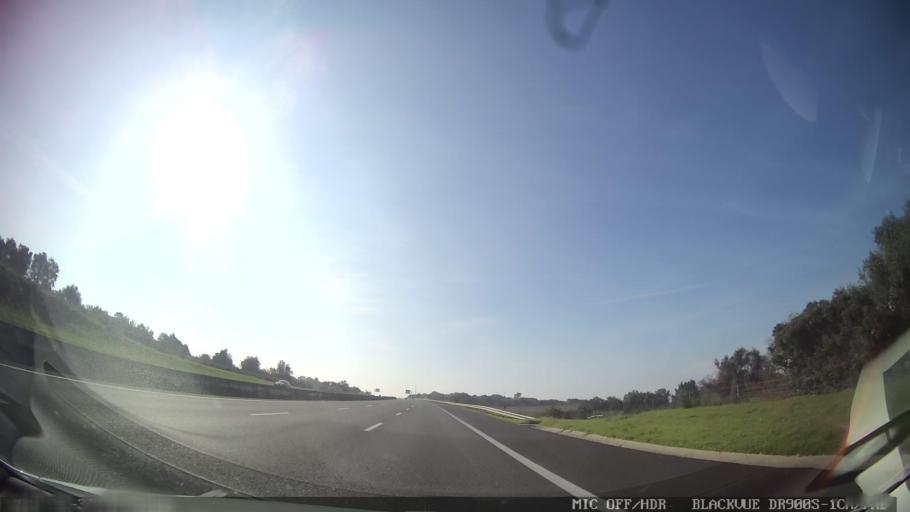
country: PT
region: Santarem
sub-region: Cartaxo
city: Cartaxo
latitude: 39.1923
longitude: -8.8196
